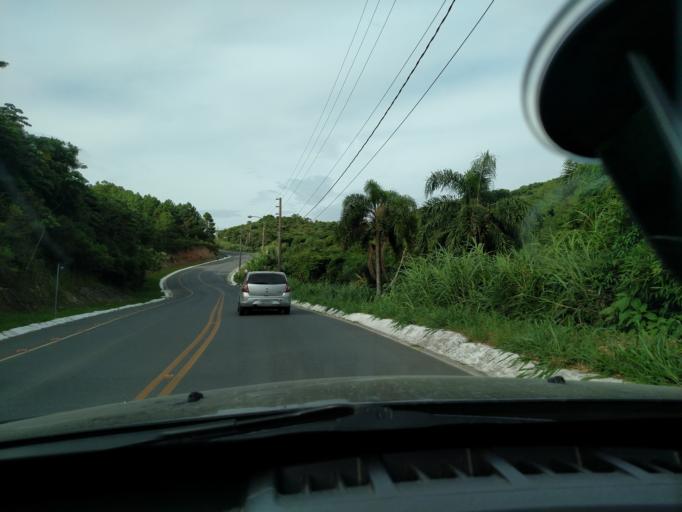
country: BR
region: Santa Catarina
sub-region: Porto Belo
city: Porto Belo
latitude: -27.1595
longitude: -48.4926
